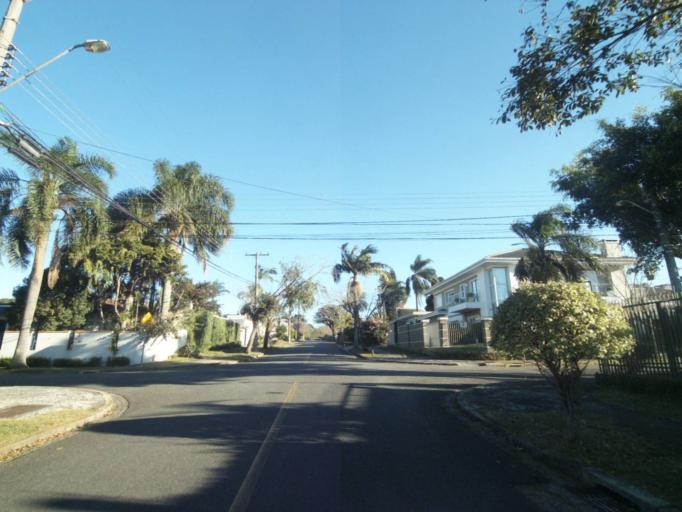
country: BR
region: Parana
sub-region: Curitiba
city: Curitiba
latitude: -25.4584
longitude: -49.2997
